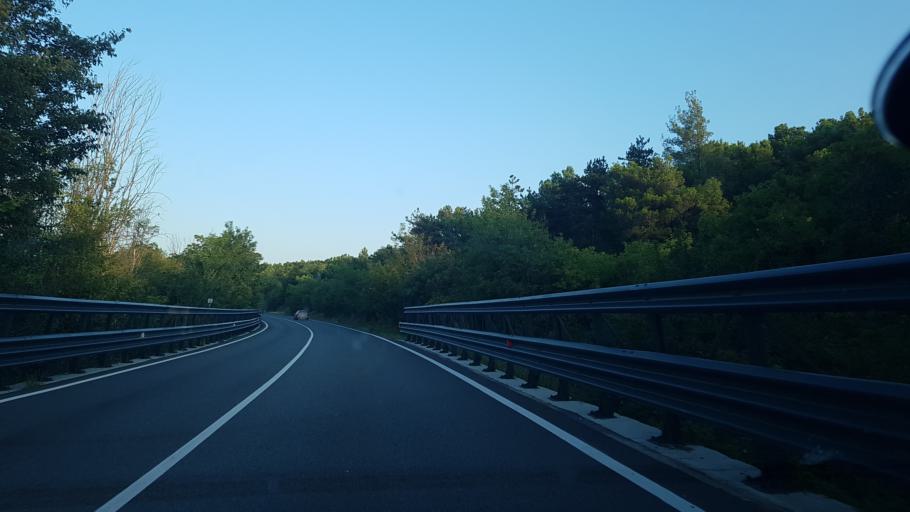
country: IT
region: Friuli Venezia Giulia
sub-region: Provincia di Trieste
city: Duino
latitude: 45.7972
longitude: 13.5809
